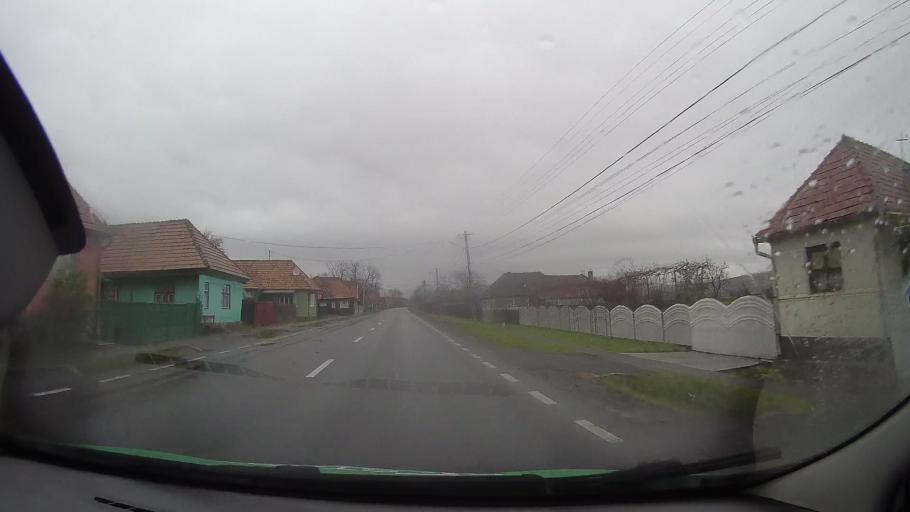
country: RO
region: Mures
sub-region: Comuna Brancovenesti
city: Valenii de Mures
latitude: 46.8845
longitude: 24.7873
